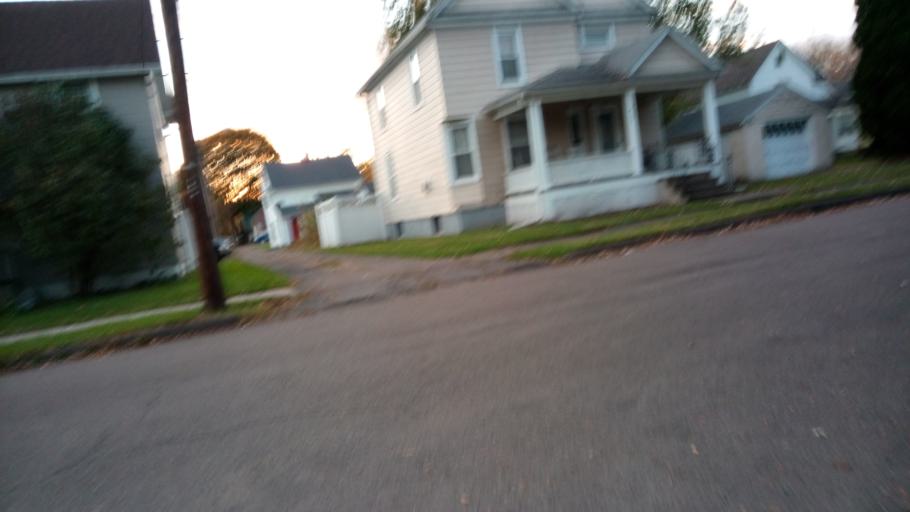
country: US
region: New York
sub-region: Chemung County
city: Elmira
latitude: 42.0749
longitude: -76.8137
